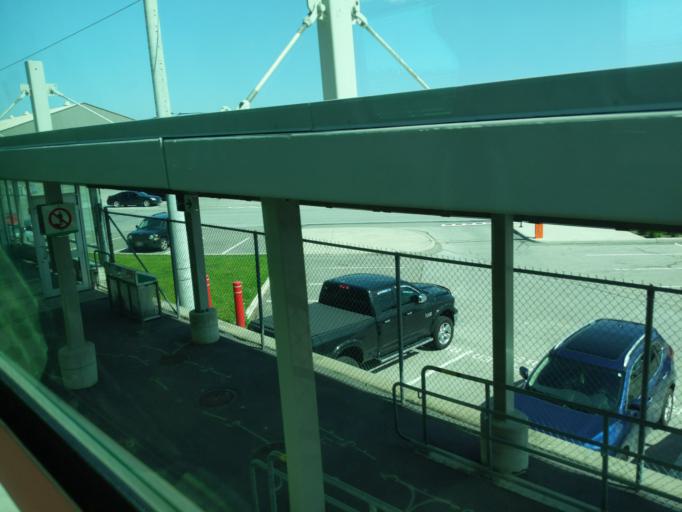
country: CA
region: Ontario
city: Etobicoke
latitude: 43.7048
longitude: -79.6383
